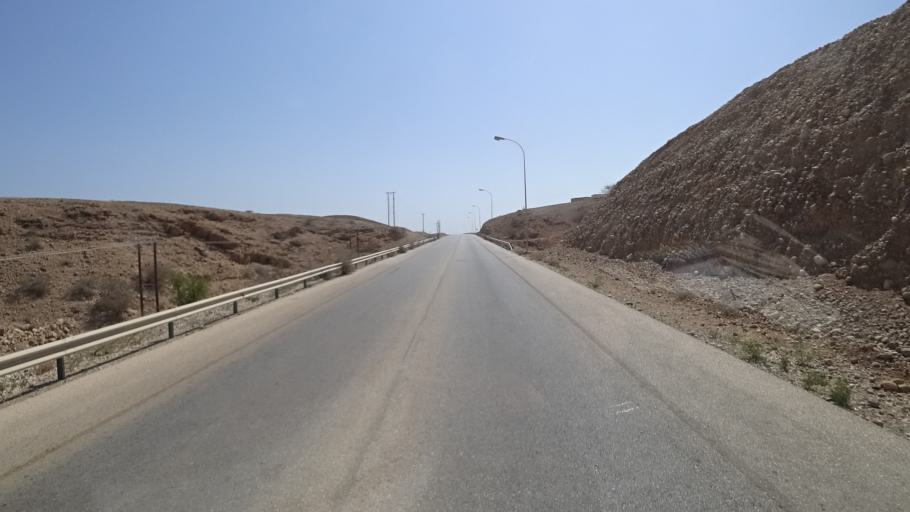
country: OM
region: Ash Sharqiyah
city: Sur
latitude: 22.5442
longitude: 59.5150
